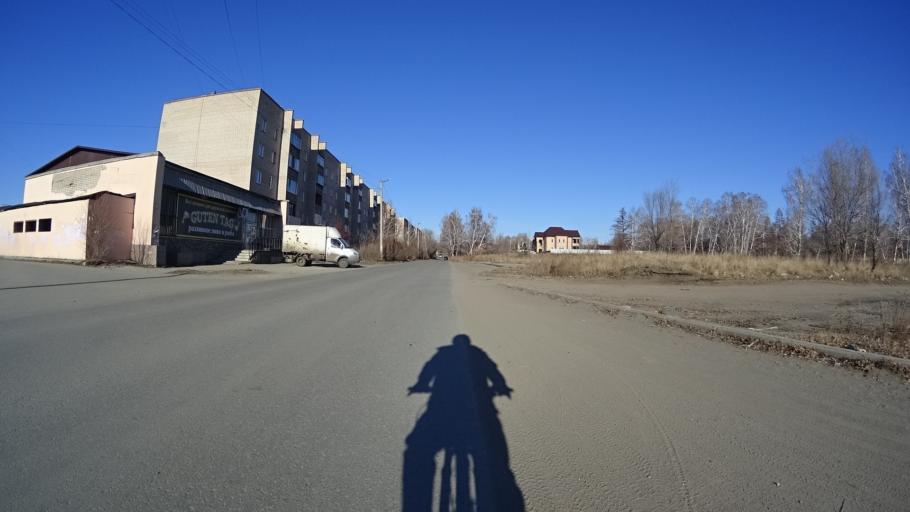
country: RU
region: Chelyabinsk
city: Troitsk
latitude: 54.0481
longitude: 61.6406
